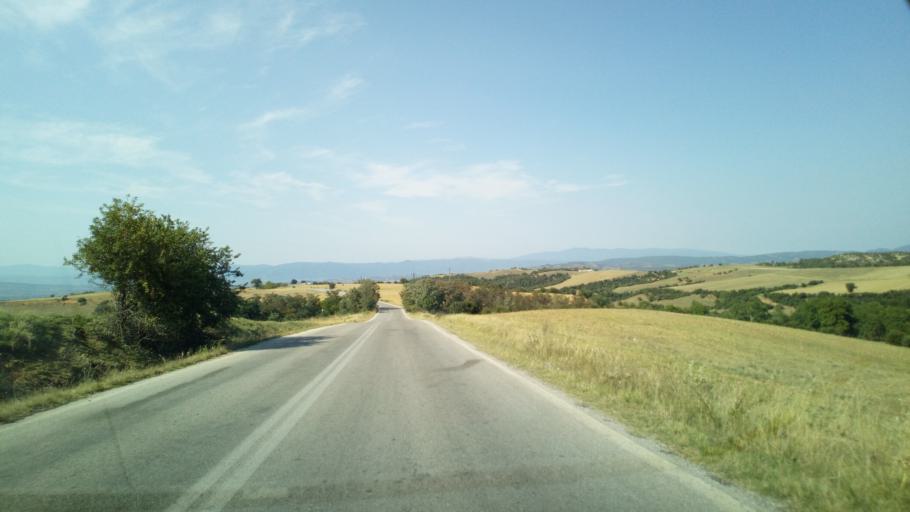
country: GR
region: Central Macedonia
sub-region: Nomos Chalkidikis
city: Arnaia
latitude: 40.5057
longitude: 23.4742
